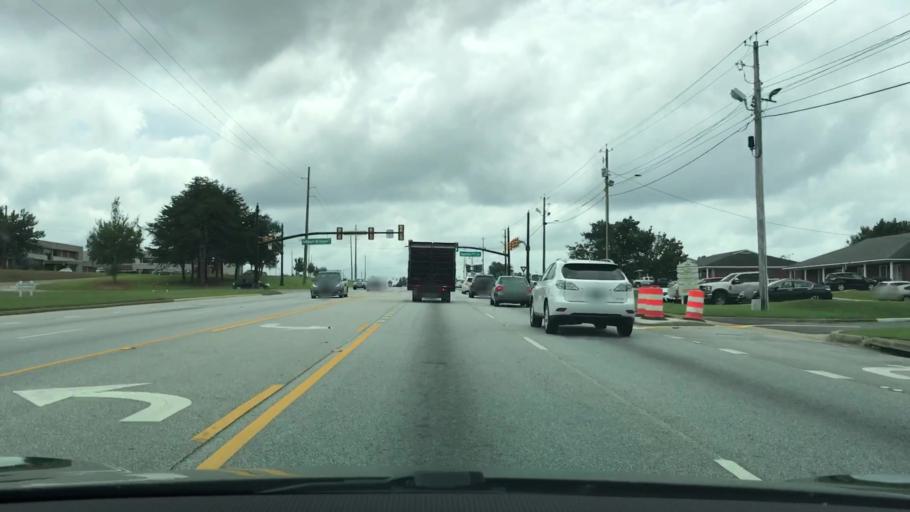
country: US
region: Alabama
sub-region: Lee County
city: Opelika
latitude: 32.6267
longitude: -85.4052
